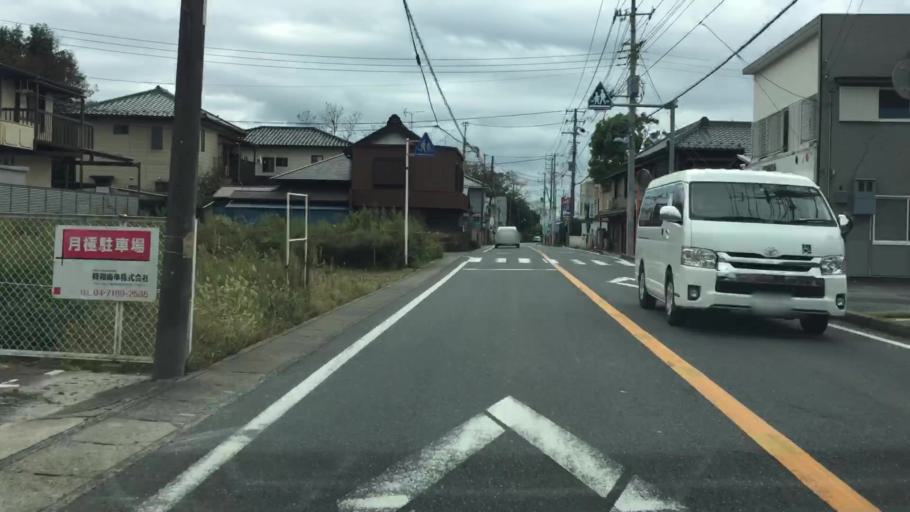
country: JP
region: Ibaraki
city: Ryugasaki
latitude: 35.8527
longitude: 140.1377
